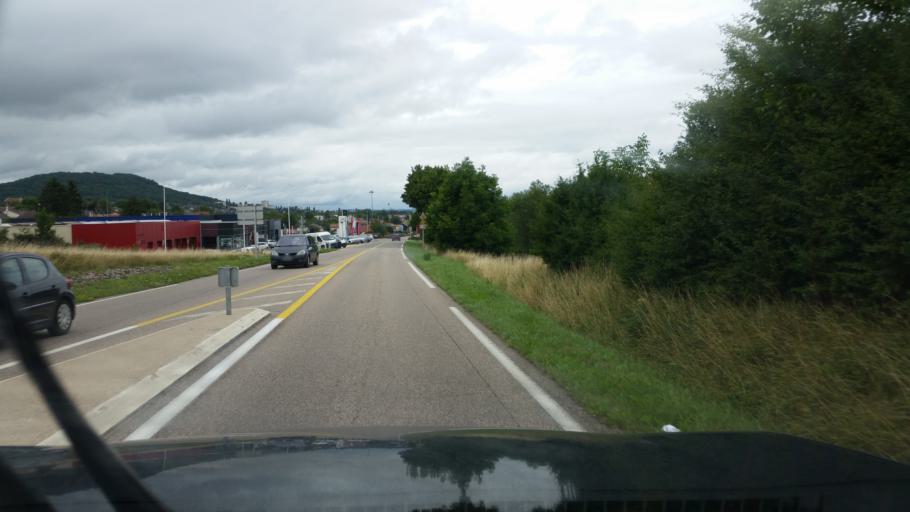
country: FR
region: Lorraine
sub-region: Departement de Meurthe-et-Moselle
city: Toul
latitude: 48.6616
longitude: 5.8780
